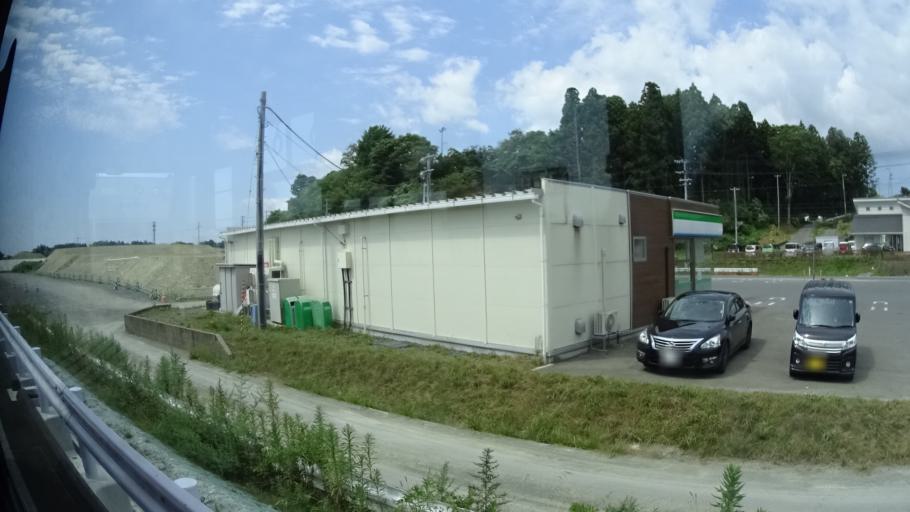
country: JP
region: Iwate
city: Ofunato
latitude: 38.8734
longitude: 141.5837
